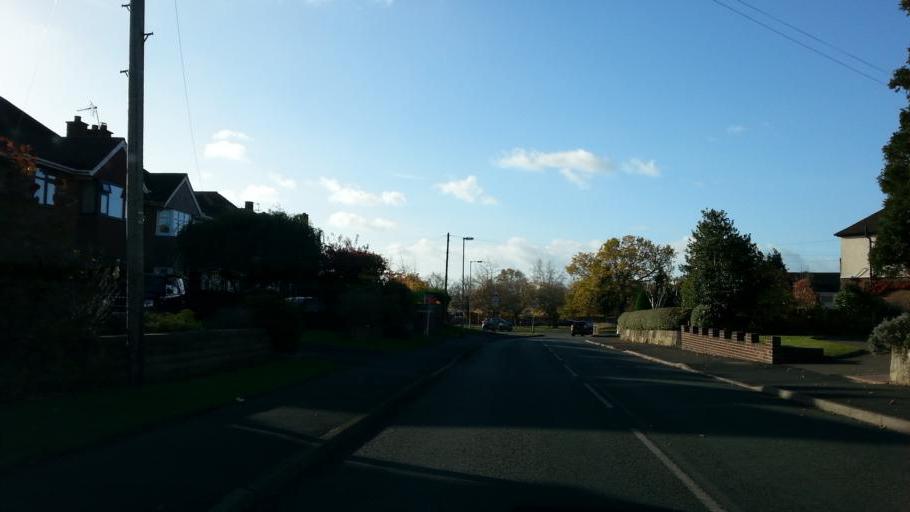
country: GB
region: England
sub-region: Staffordshire
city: Cannock
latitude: 52.6856
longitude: -2.0413
